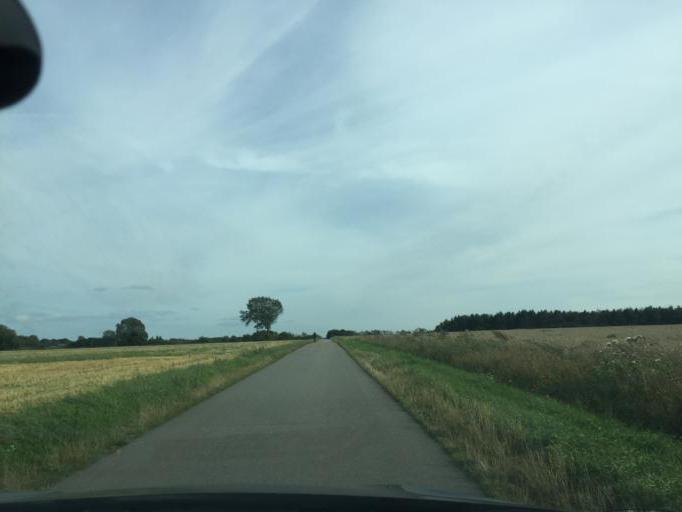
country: DK
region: South Denmark
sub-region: Kerteminde Kommune
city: Langeskov
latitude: 55.3372
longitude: 10.5515
